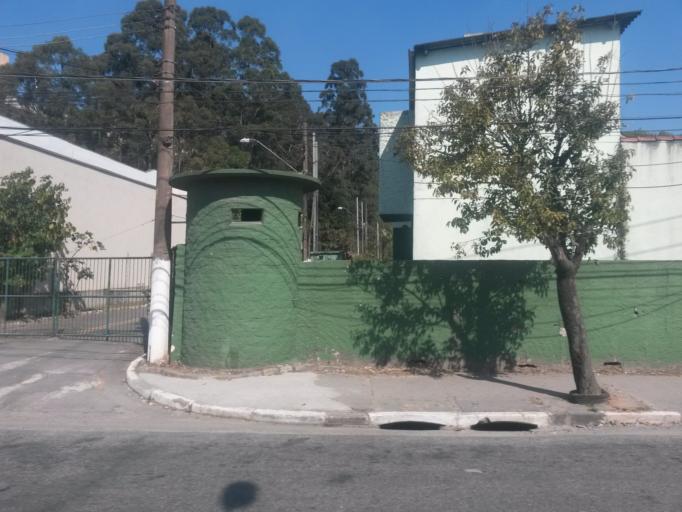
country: BR
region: Sao Paulo
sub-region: Sao Bernardo Do Campo
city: Sao Bernardo do Campo
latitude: -23.7389
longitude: -46.5305
